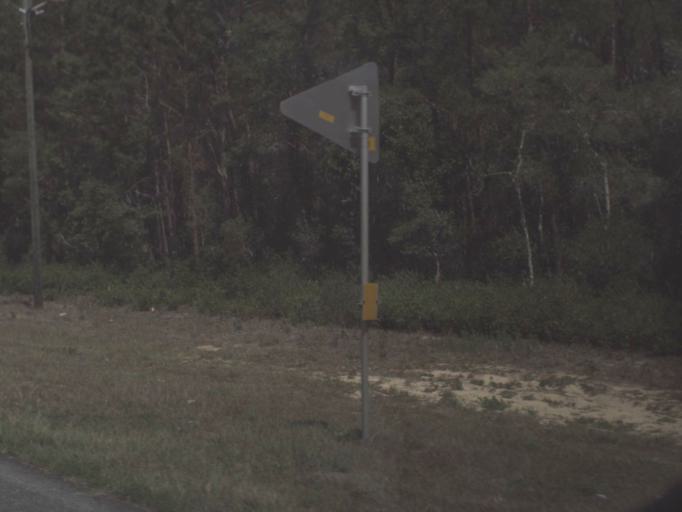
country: US
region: Florida
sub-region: Marion County
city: Silver Springs Shores
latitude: 29.1770
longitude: -81.7907
